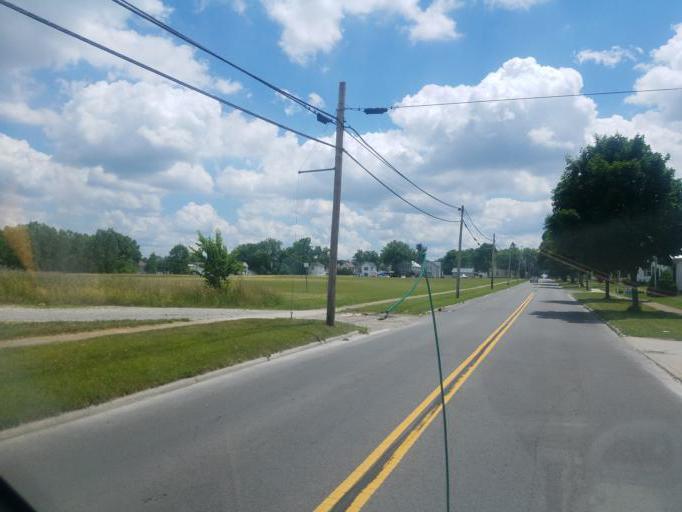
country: US
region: Ohio
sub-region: Huron County
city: Willard
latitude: 41.0604
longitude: -82.7331
